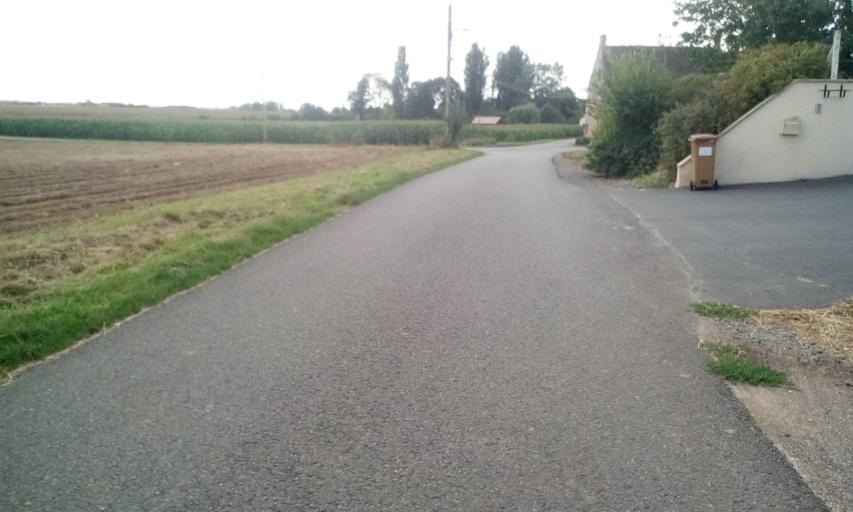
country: FR
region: Lower Normandy
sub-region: Departement du Calvados
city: Saint-Sylvain
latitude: 49.0721
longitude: -0.1975
